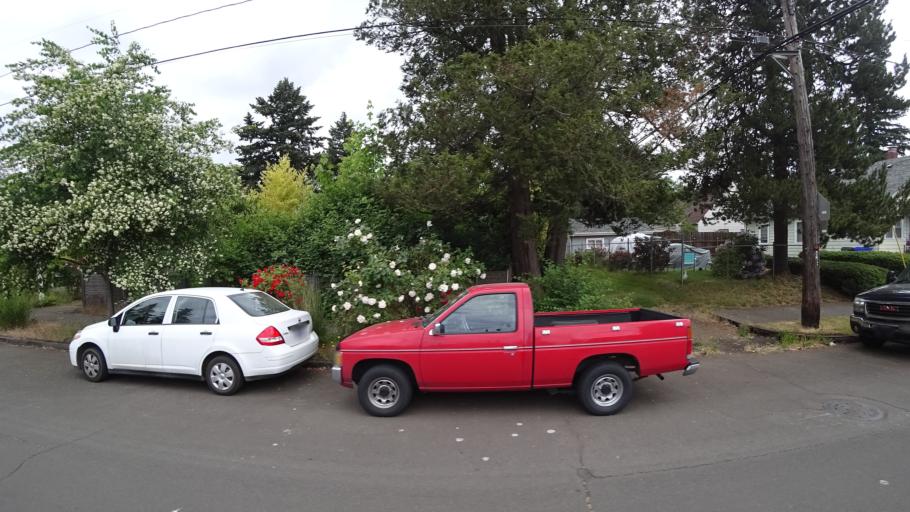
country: US
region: Oregon
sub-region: Washington County
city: West Haven
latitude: 45.5777
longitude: -122.7285
